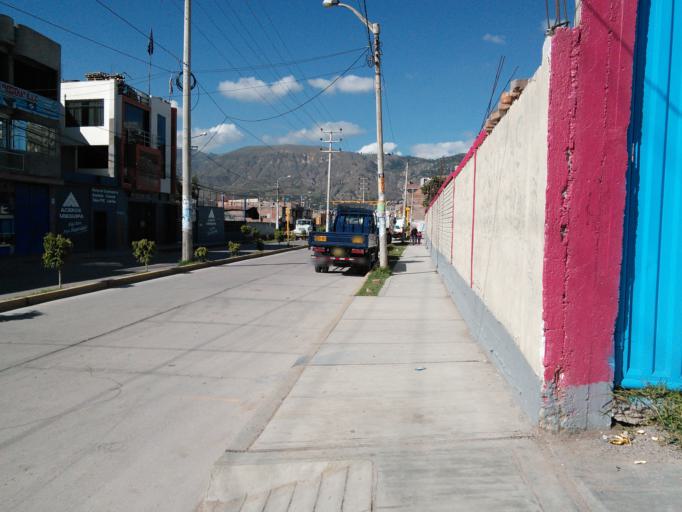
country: PE
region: Ayacucho
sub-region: Provincia de Huamanga
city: Ayacucho
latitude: -13.1531
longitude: -74.2162
